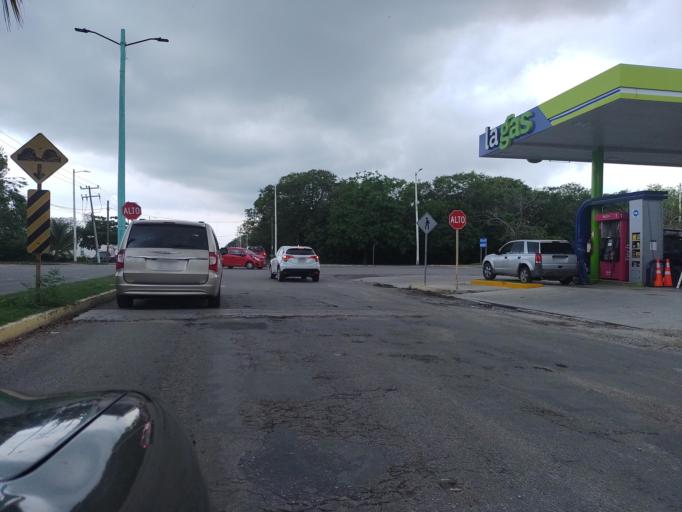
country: MX
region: Quintana Roo
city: Chetumal
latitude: 18.5137
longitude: -88.2797
